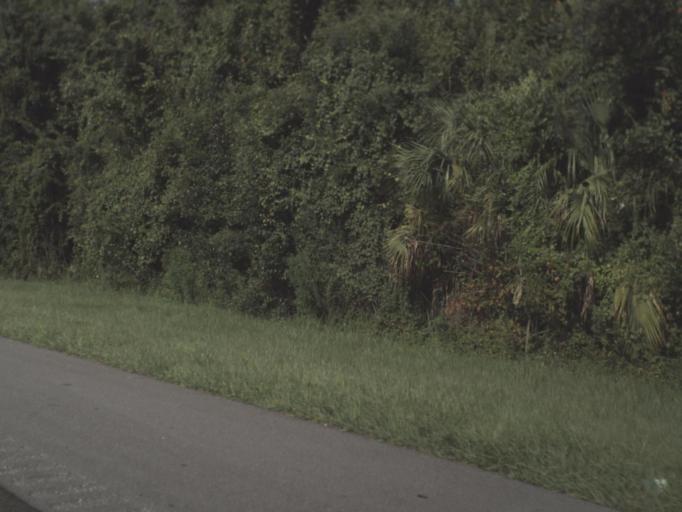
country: US
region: Florida
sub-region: Hillsborough County
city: Lutz
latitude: 28.1312
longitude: -82.4155
